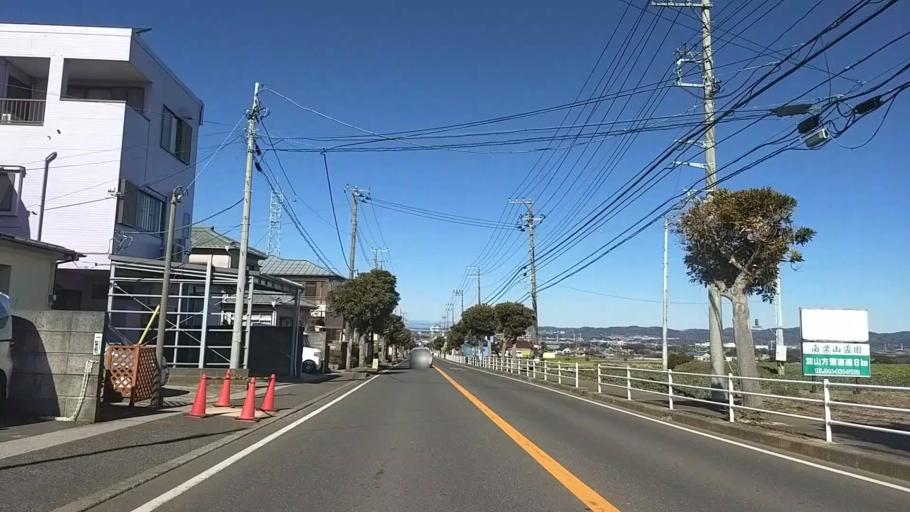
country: JP
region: Kanagawa
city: Miura
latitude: 35.1703
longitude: 139.6384
